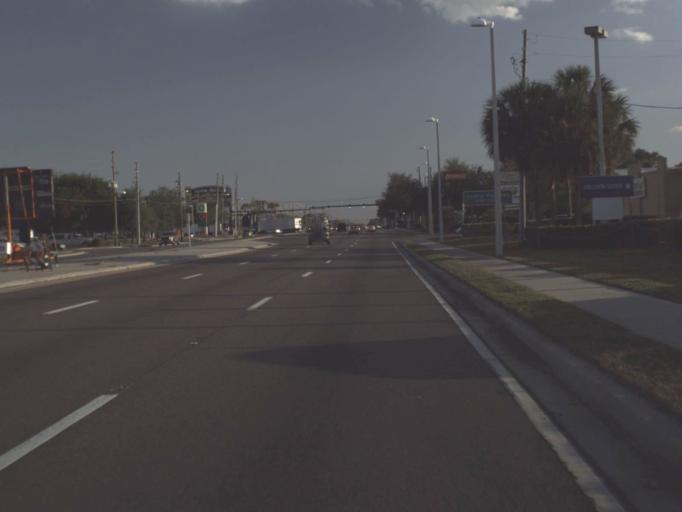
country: US
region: Florida
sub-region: Orange County
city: Southchase
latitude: 28.4099
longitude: -81.4048
